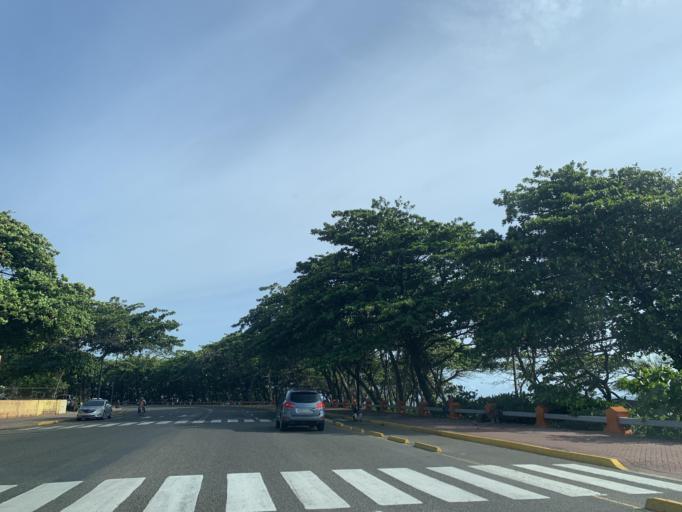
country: DO
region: Puerto Plata
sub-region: Puerto Plata
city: Puerto Plata
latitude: 19.7969
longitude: -70.6852
